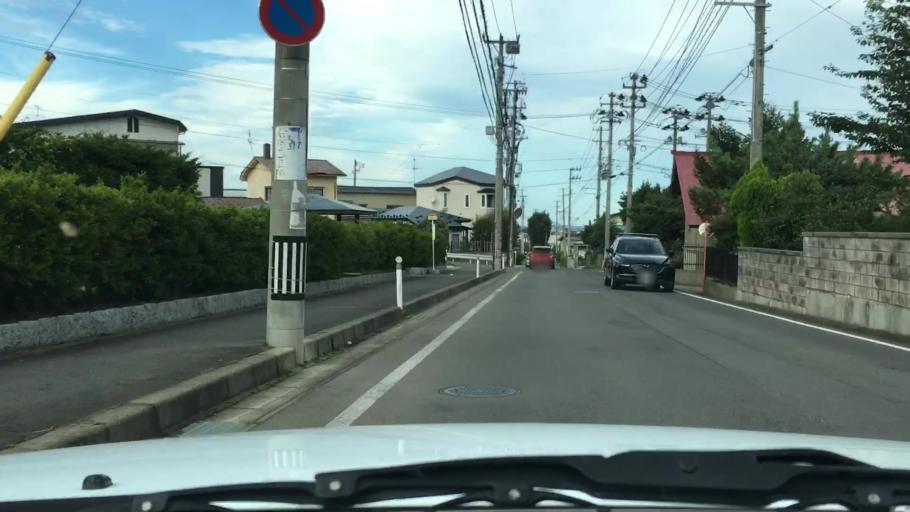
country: JP
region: Aomori
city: Hirosaki
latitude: 40.5832
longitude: 140.4596
